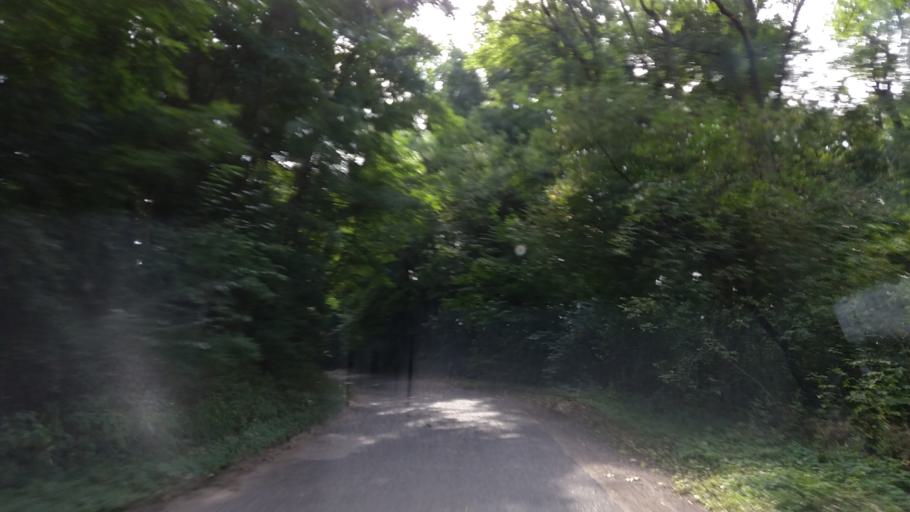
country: PL
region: West Pomeranian Voivodeship
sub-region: Powiat stargardzki
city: Suchan
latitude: 53.2333
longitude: 15.3538
